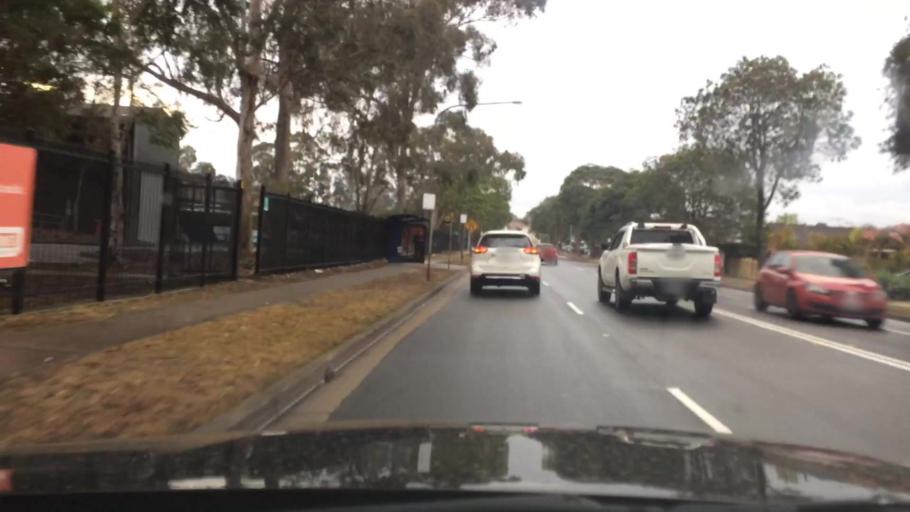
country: AU
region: New South Wales
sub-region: Fairfield
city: Fairfield Heights
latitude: -33.8509
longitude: 150.9137
